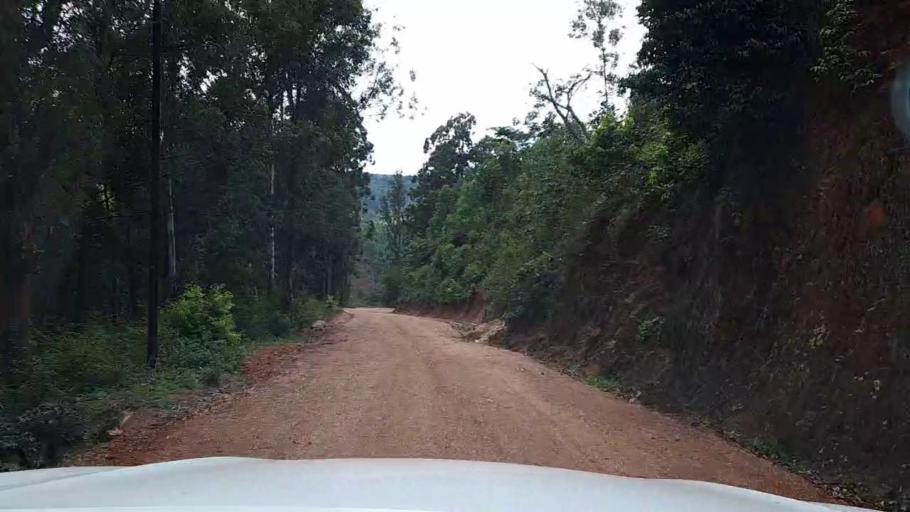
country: BI
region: Ngozi
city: Ngozi
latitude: -2.8120
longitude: 29.7300
